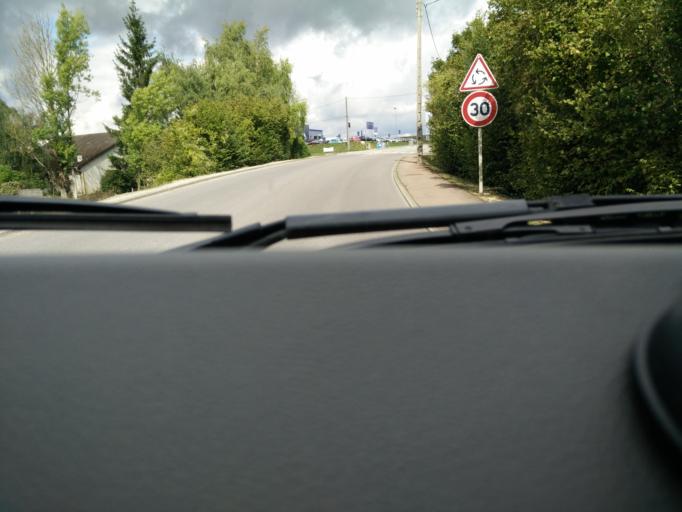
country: FR
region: Lorraine
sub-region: Departement de la Meuse
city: Belleville-sur-Meuse
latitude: 49.1789
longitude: 5.3700
